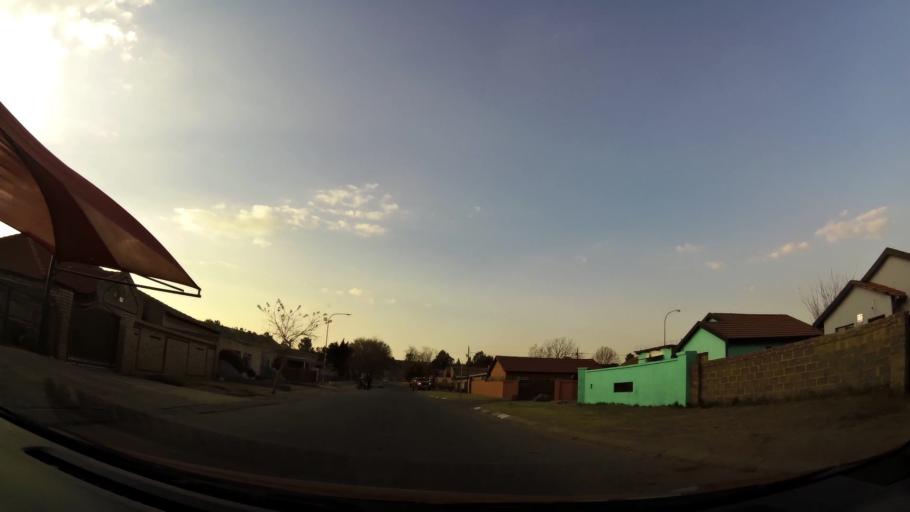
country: ZA
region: Gauteng
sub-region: City of Johannesburg Metropolitan Municipality
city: Roodepoort
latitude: -26.2098
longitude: 27.8955
